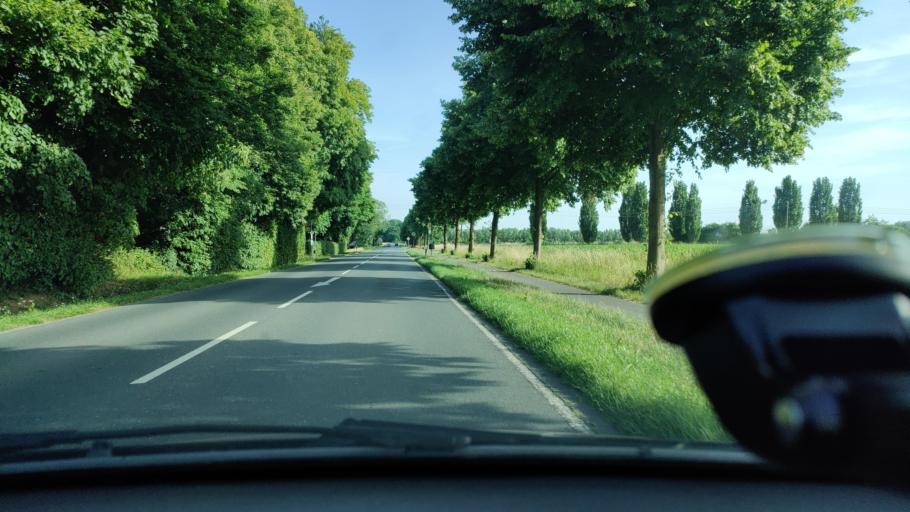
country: DE
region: North Rhine-Westphalia
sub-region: Regierungsbezirk Munster
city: Coesfeld
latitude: 51.9793
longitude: 7.1921
